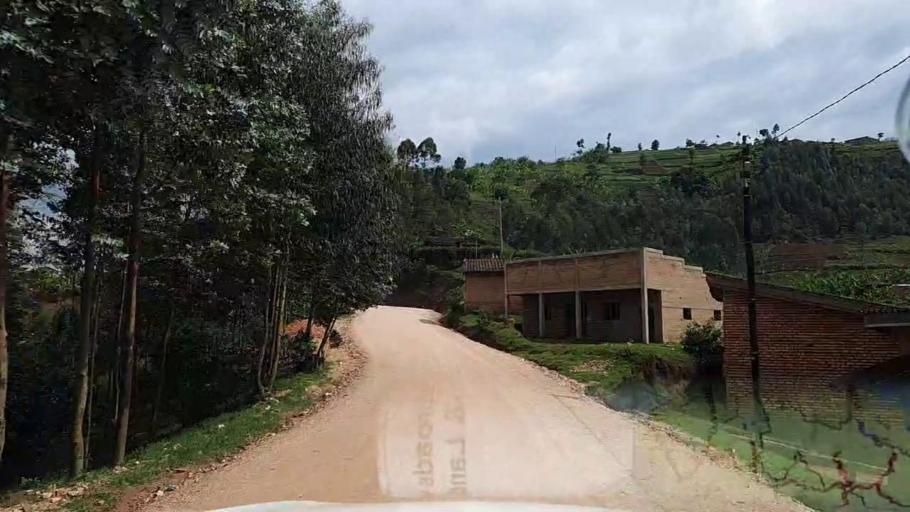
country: RW
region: Southern Province
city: Nzega
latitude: -2.3374
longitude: 29.4446
